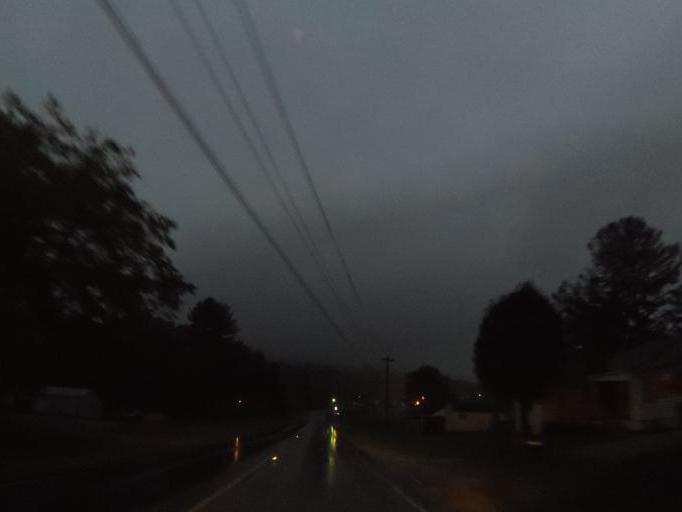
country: US
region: North Carolina
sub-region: Alleghany County
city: Sparta
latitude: 36.5317
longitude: -81.1602
